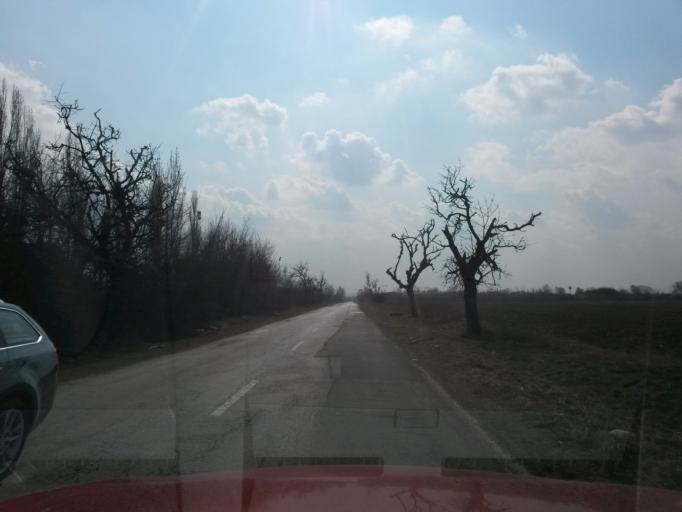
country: SK
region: Kosicky
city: Kosice
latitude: 48.6104
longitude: 21.1760
